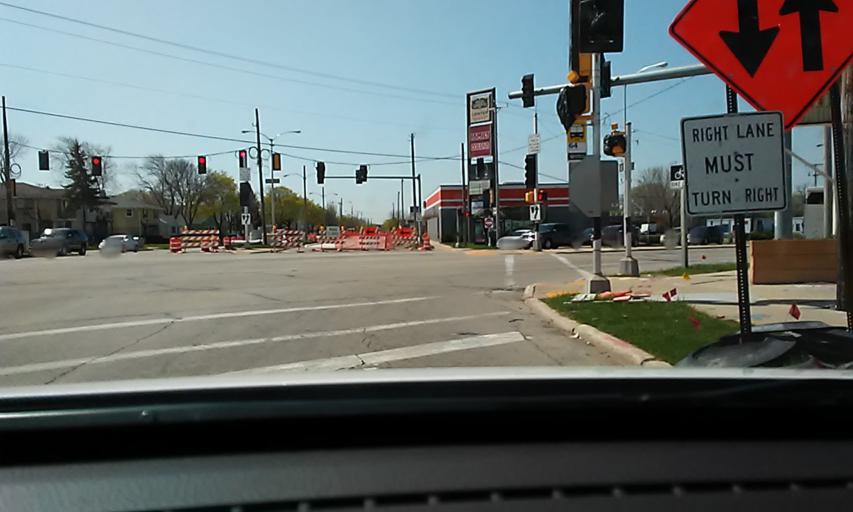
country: US
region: Wisconsin
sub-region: Milwaukee County
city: Greenfield
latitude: 42.9771
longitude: -87.9880
